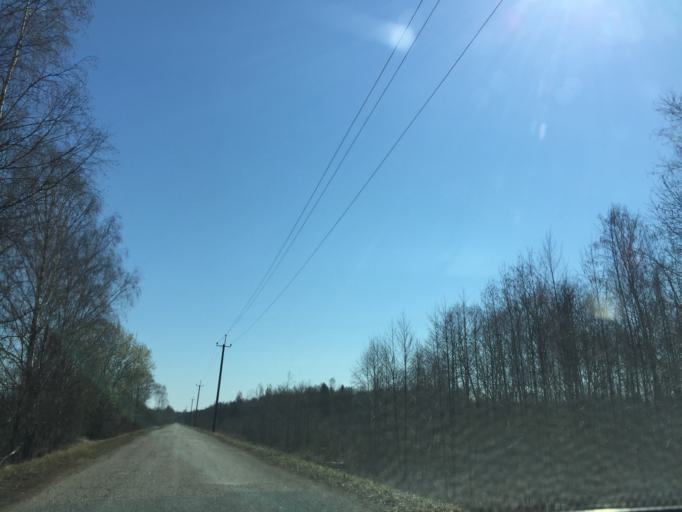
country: EE
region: Jogevamaa
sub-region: Mustvee linn
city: Mustvee
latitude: 58.7799
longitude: 26.9363
